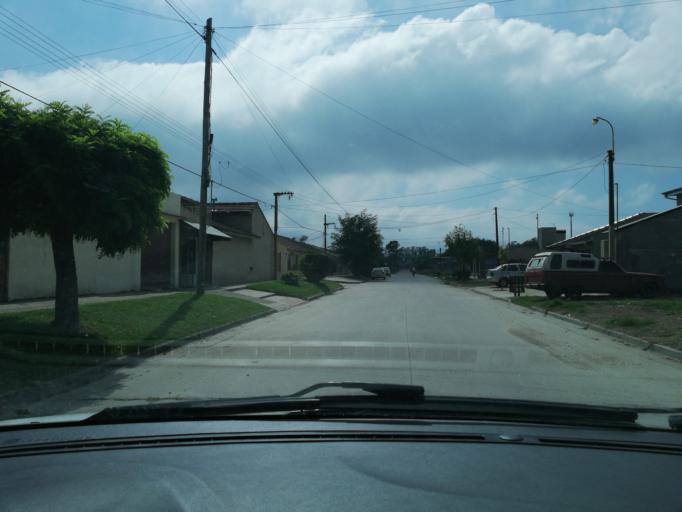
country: AR
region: Buenos Aires
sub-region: Partido de Balcarce
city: Balcarce
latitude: -37.8500
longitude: -58.2429
